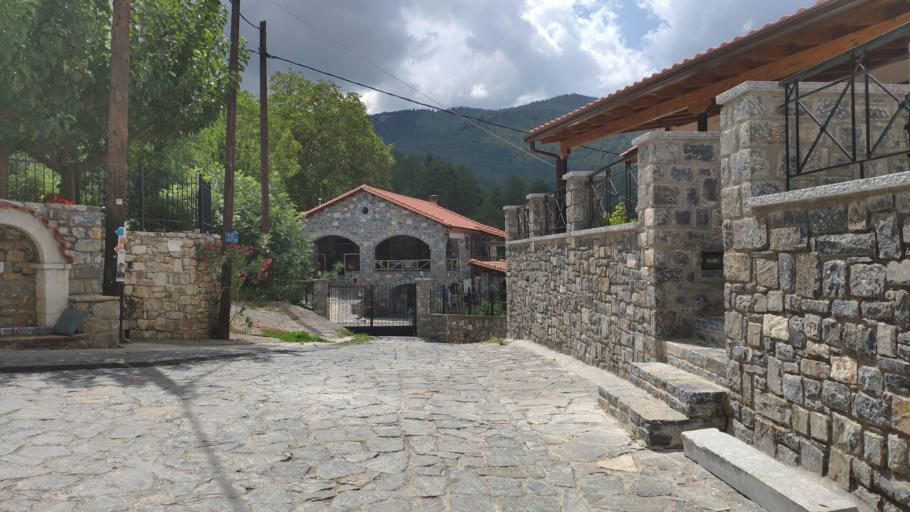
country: GR
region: Peloponnese
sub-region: Nomos Lakonias
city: Kariai
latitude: 37.2432
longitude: 22.5512
